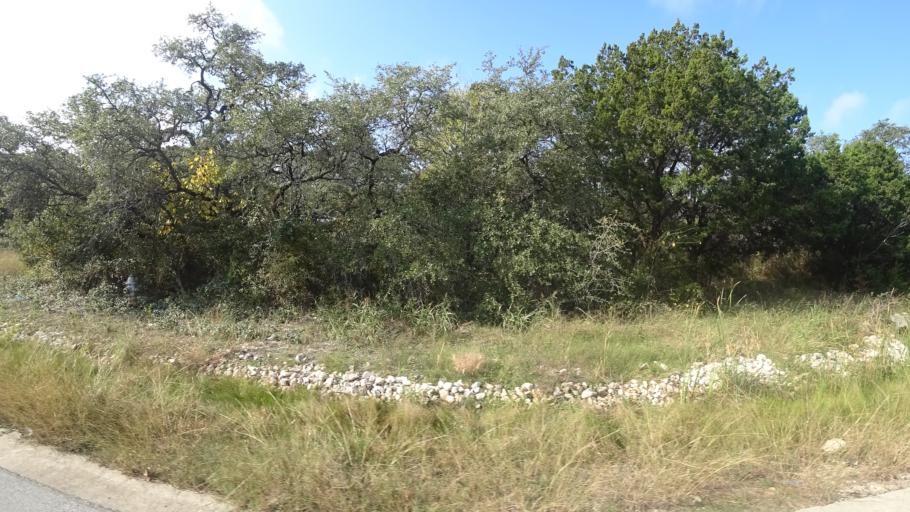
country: US
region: Texas
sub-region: Travis County
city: Bee Cave
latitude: 30.3075
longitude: -97.9340
